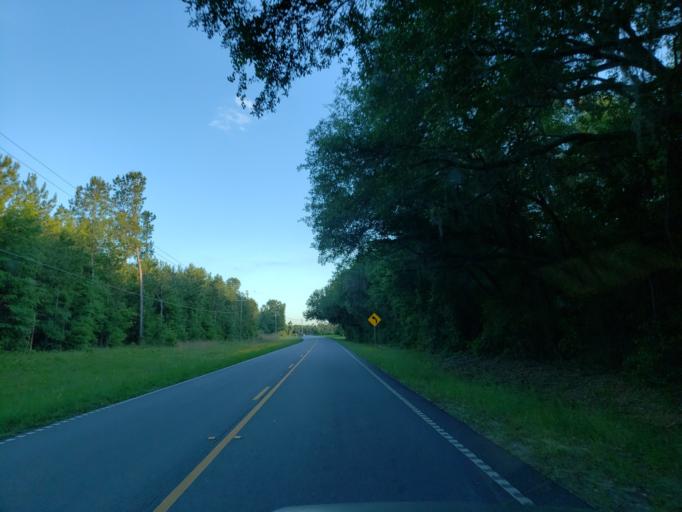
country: US
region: Georgia
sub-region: Lowndes County
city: Valdosta
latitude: 30.7284
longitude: -83.2482
